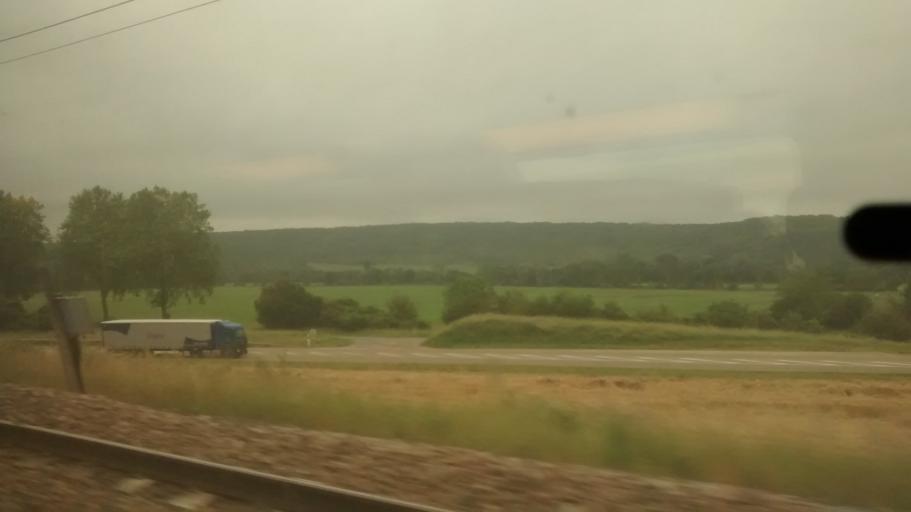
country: FR
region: Bourgogne
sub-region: Departement de l'Yonne
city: Malay-le-Grand
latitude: 48.1781
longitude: 3.3556
